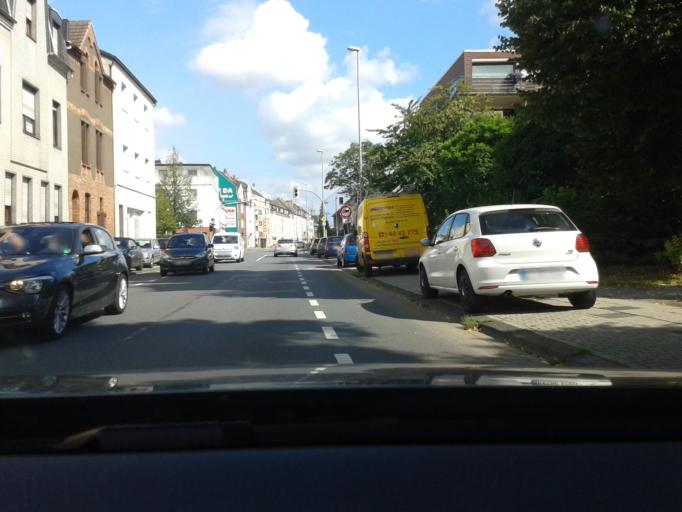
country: DE
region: North Rhine-Westphalia
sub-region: Regierungsbezirk Dusseldorf
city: Oberhausen
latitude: 51.4586
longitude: 6.8512
